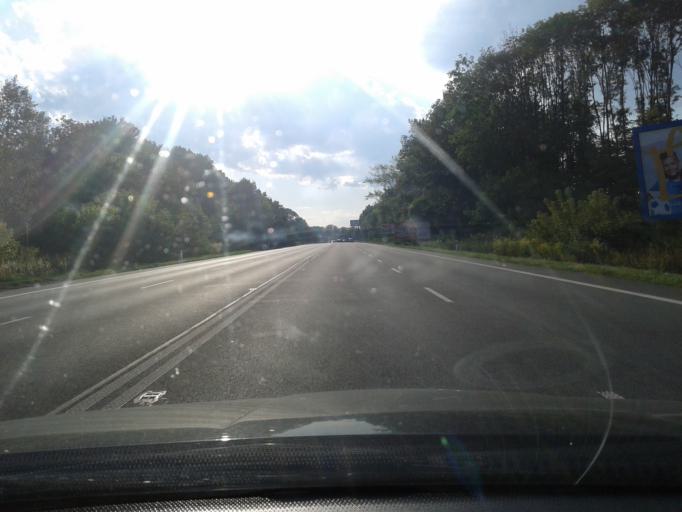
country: CZ
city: Vratimov
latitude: 49.8054
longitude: 18.3151
